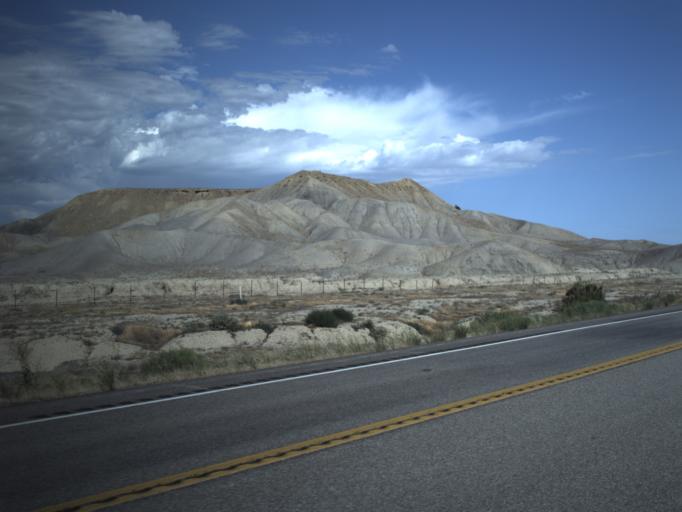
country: US
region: Utah
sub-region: Carbon County
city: East Carbon City
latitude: 39.2868
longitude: -110.3512
